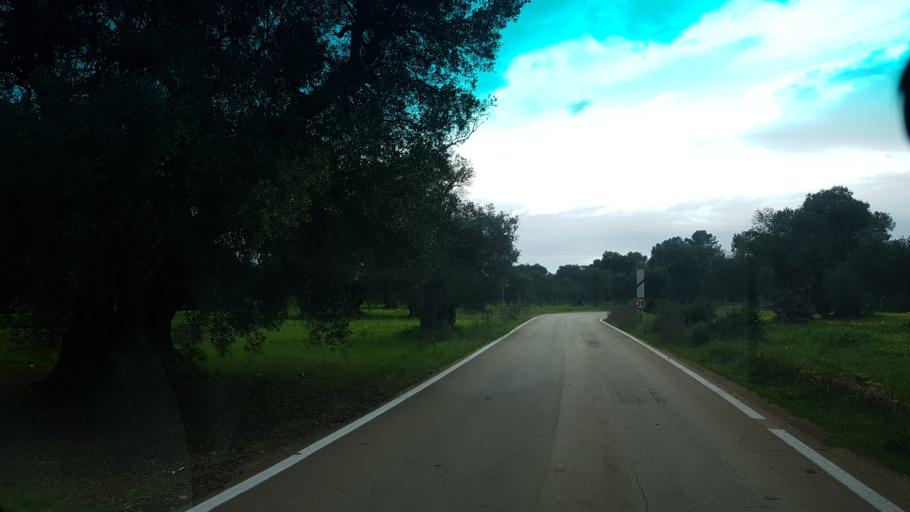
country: IT
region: Apulia
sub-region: Provincia di Brindisi
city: San Vito dei Normanni
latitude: 40.7013
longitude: 17.7638
